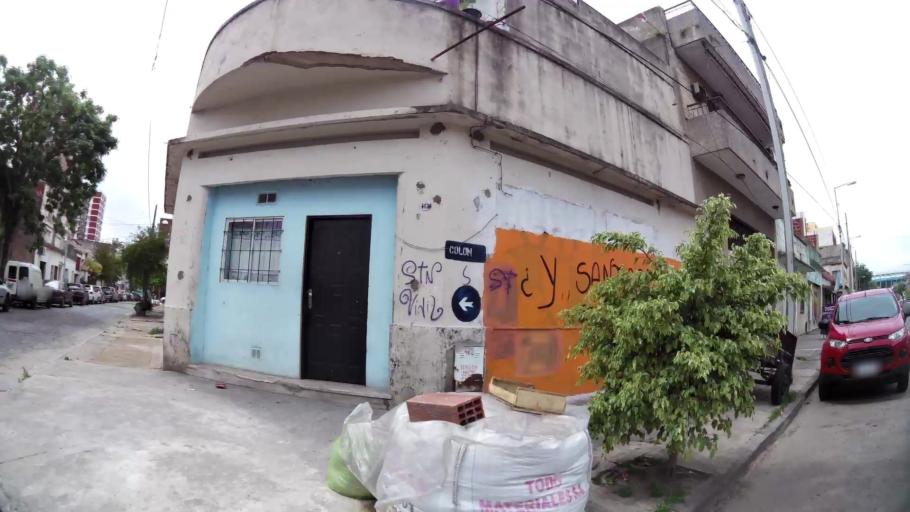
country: AR
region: Buenos Aires
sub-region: Partido de Avellaneda
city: Avellaneda
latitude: -34.6635
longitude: -58.3712
